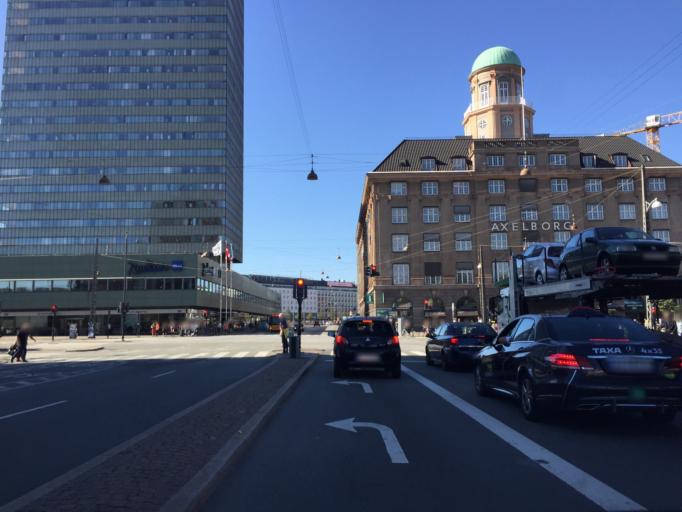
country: DK
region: Capital Region
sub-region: Kobenhavn
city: Copenhagen
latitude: 55.6742
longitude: 12.5650
